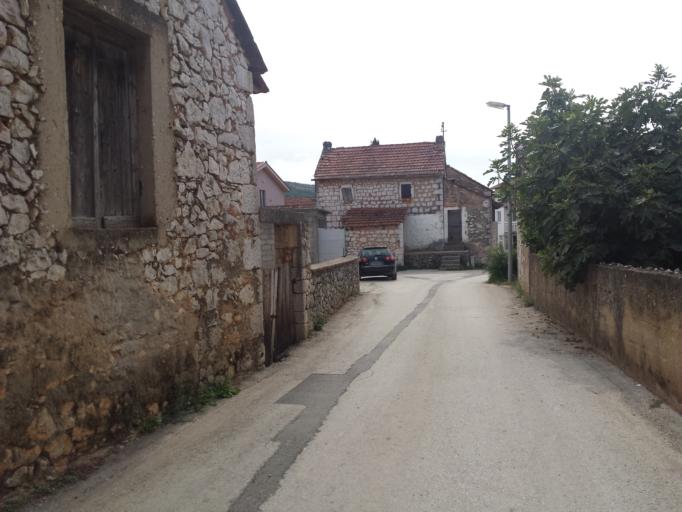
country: BA
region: Federation of Bosnia and Herzegovina
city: Citluk
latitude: 43.1939
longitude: 17.6735
